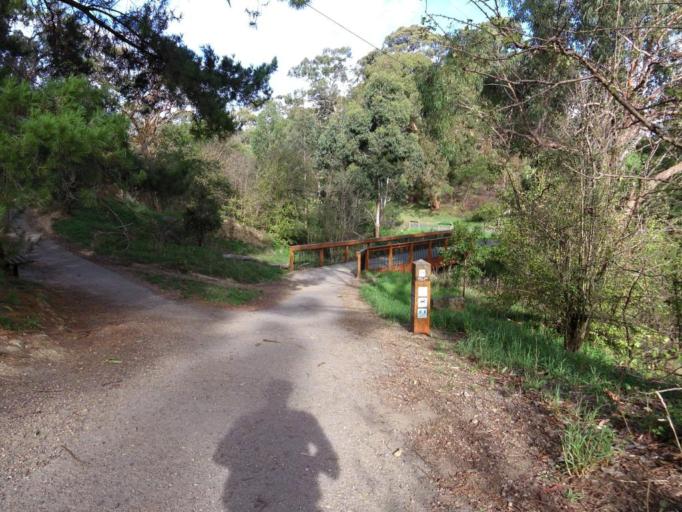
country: AU
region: Victoria
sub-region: Manningham
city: Doncaster East
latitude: -37.7766
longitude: 145.1396
